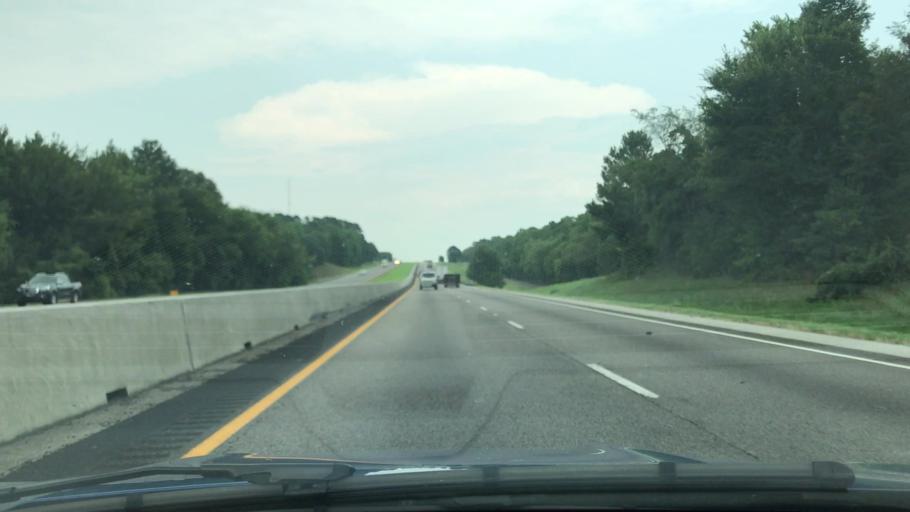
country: US
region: Texas
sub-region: Gregg County
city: Liberty City
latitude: 32.4379
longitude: -95.0315
